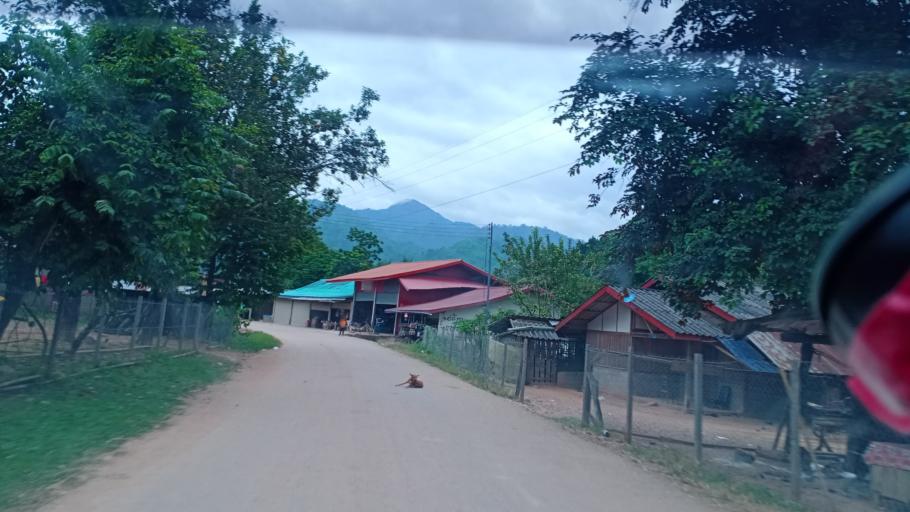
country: TH
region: Changwat Bueng Kan
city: Pak Khat
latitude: 18.7125
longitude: 103.2120
